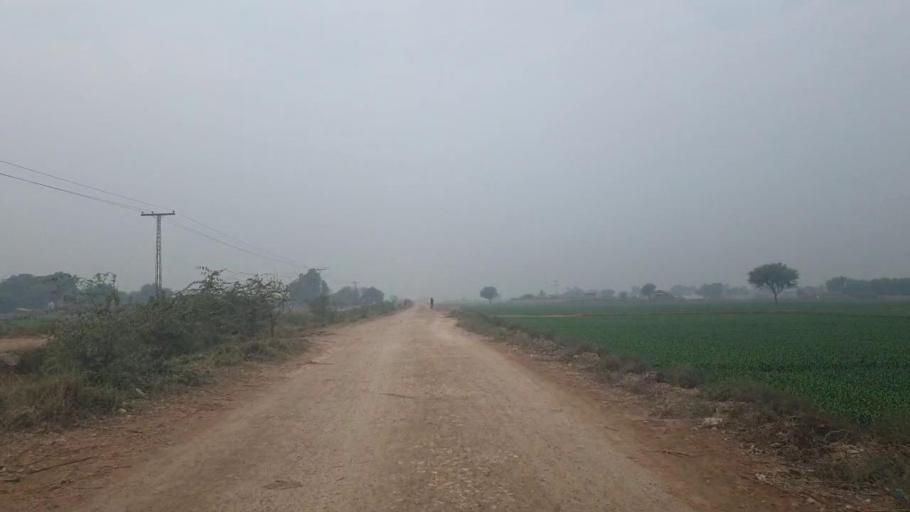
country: PK
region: Sindh
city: Tando Adam
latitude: 25.6898
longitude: 68.6690
